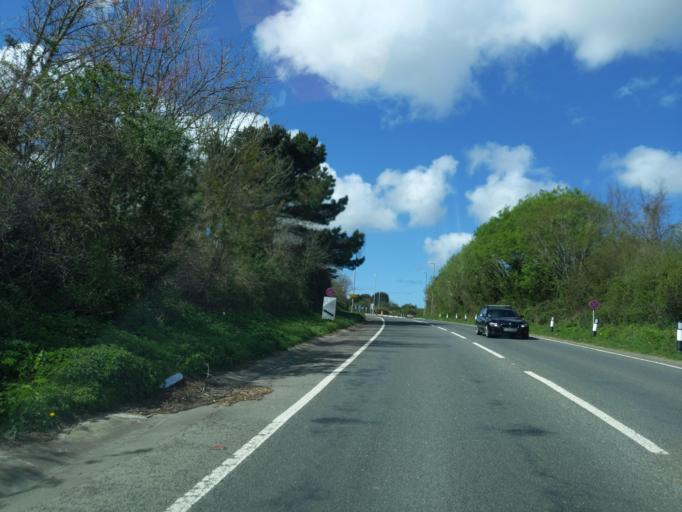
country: GB
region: England
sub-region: Cornwall
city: Wadebridge
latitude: 50.5218
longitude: -4.8209
